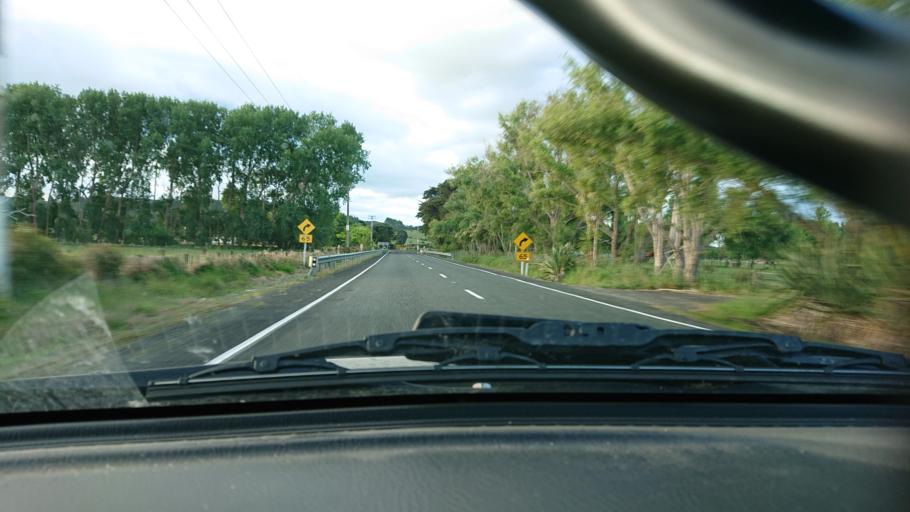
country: NZ
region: Auckland
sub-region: Auckland
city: Parakai
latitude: -36.4973
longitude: 174.4499
